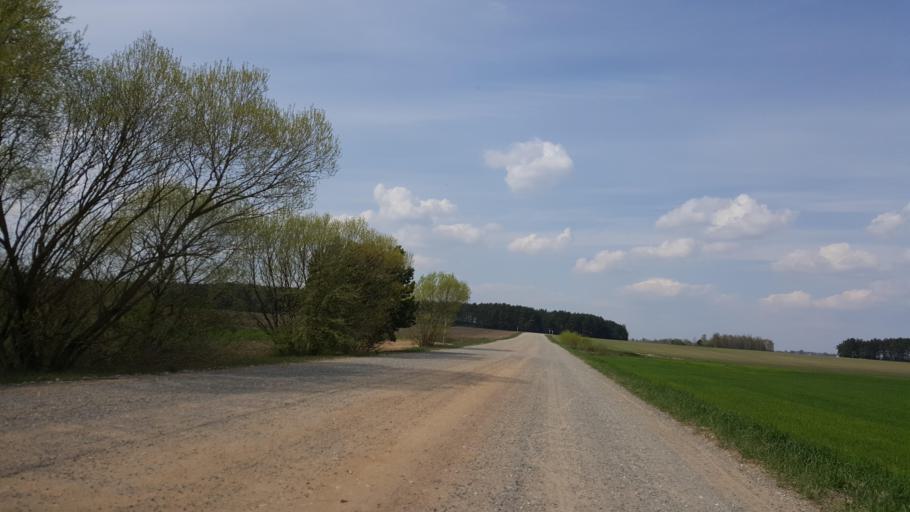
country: BY
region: Brest
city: Zhabinka
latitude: 52.2255
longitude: 23.9167
